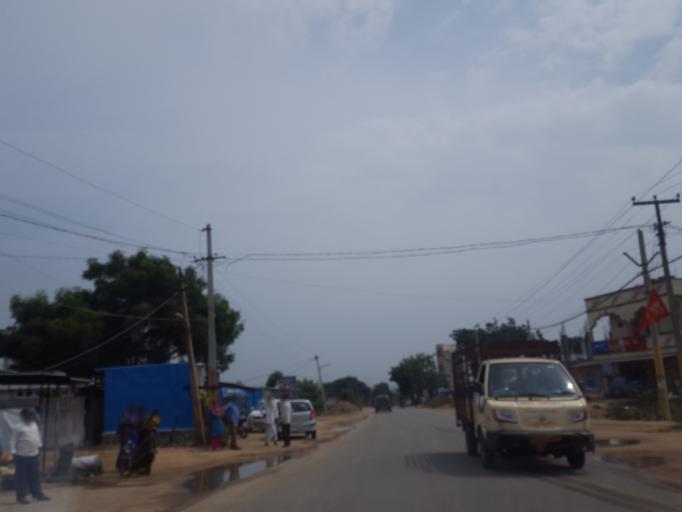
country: IN
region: Telangana
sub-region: Medak
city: Patancheru
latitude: 17.5046
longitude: 78.2004
